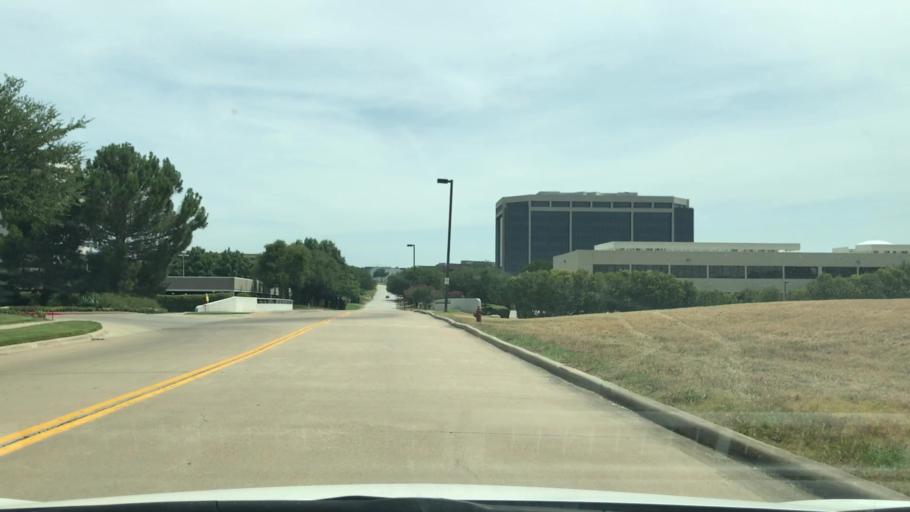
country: US
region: Texas
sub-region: Dallas County
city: Coppell
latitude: 32.8914
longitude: -96.9715
